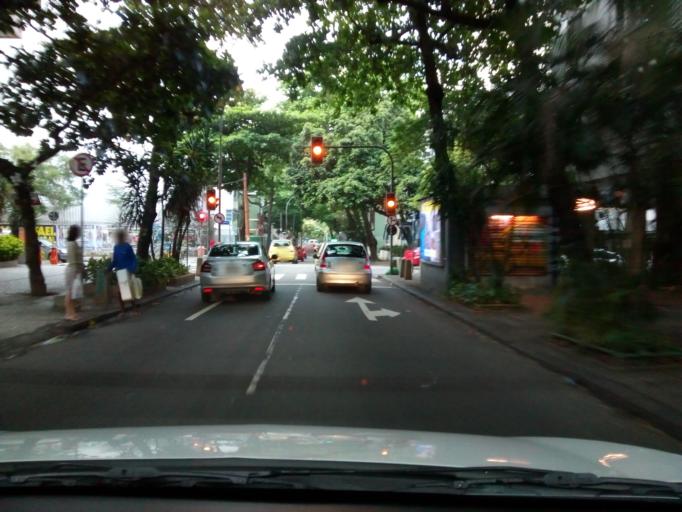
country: BR
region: Rio de Janeiro
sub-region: Rio De Janeiro
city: Rio de Janeiro
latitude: -22.9816
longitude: -43.2027
